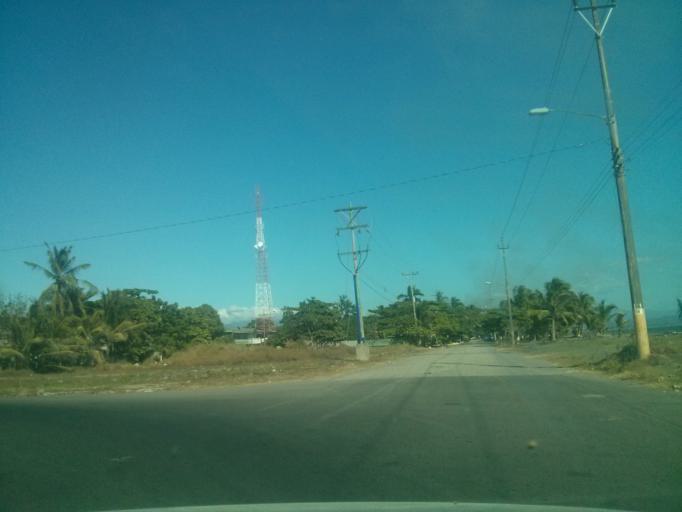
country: CR
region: Puntarenas
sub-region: Canton Central de Puntarenas
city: Puntarenas
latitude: 9.9773
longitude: -84.8252
